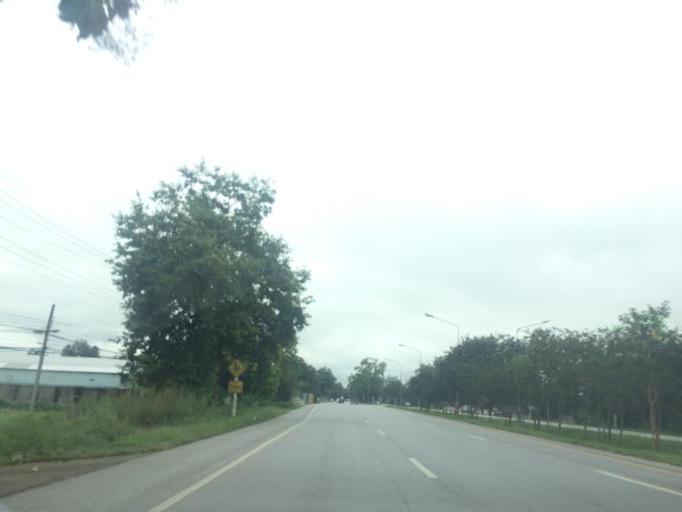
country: TH
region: Chiang Rai
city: Mae Lao
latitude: 19.7684
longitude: 99.7366
